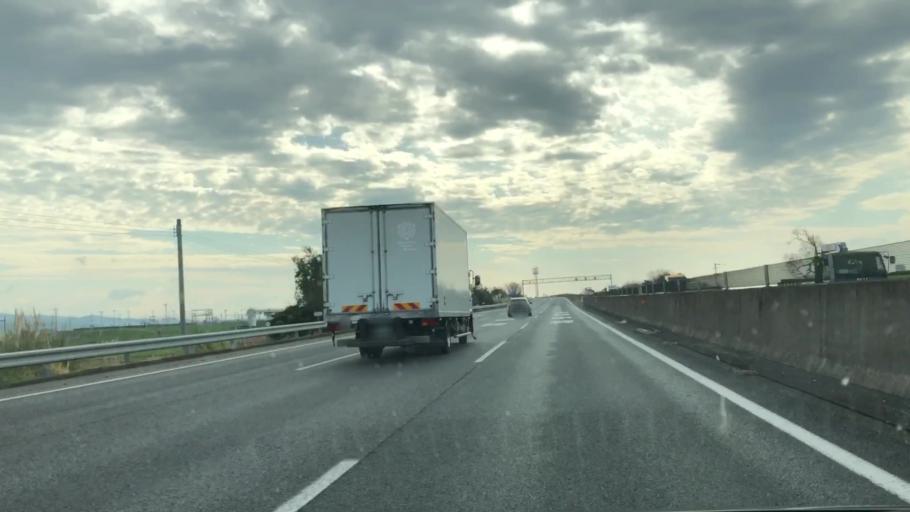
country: JP
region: Saga Prefecture
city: Tosu
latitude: 33.3593
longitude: 130.5399
